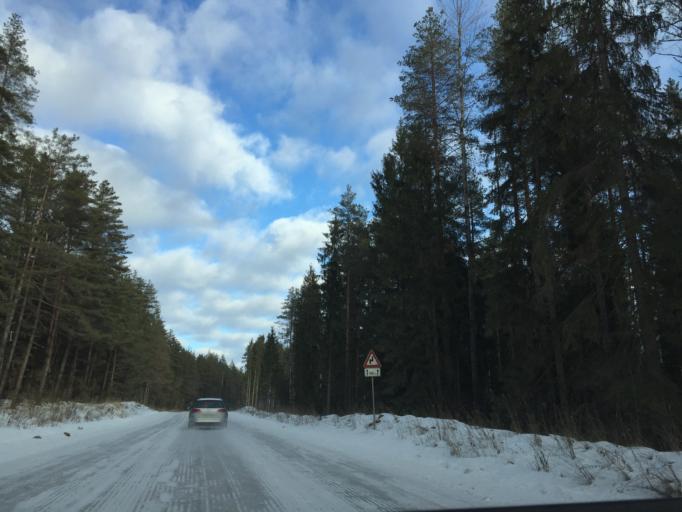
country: LV
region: Ogre
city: Jumprava
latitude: 56.5725
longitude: 24.9369
